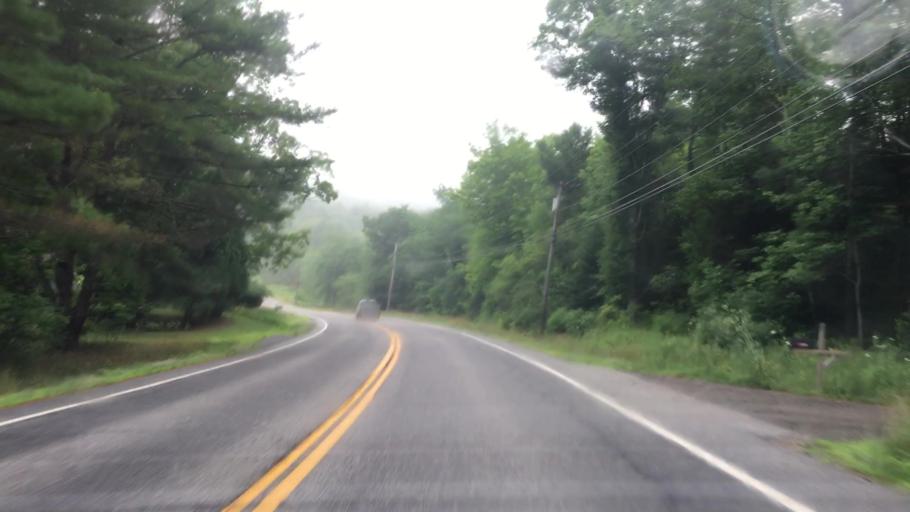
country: US
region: Maine
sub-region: Lincoln County
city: Edgecomb
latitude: 43.9793
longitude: -69.6385
